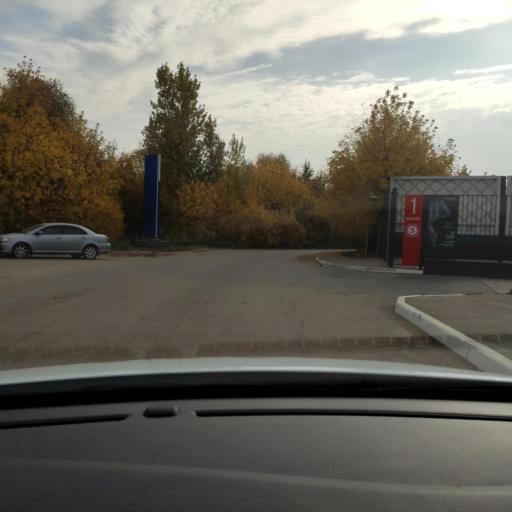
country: RU
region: Tatarstan
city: Verkhniy Uslon
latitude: 55.8038
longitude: 49.0476
